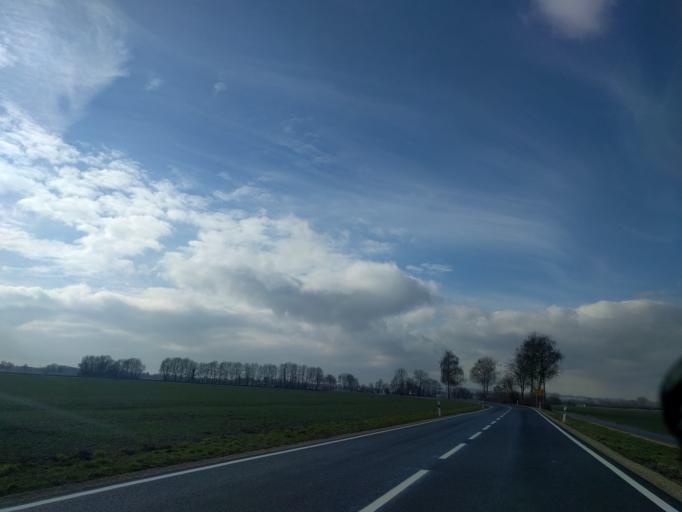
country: DE
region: Bavaria
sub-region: Swabia
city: Asbach-Baumenheim
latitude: 48.7077
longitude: 10.8213
